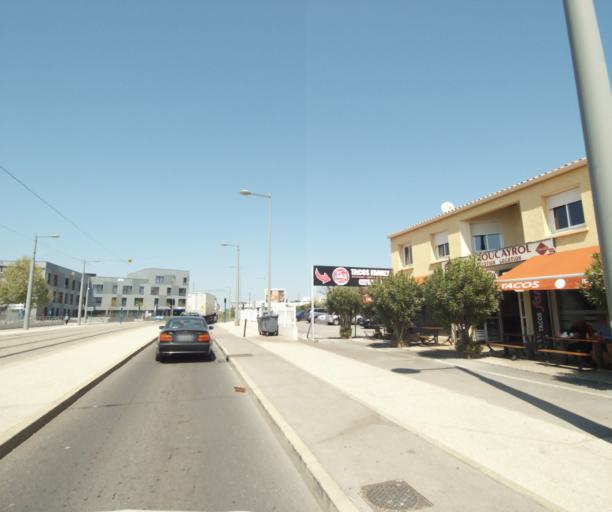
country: FR
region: Languedoc-Roussillon
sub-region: Departement de l'Herault
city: Juvignac
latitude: 43.6163
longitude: 3.8260
